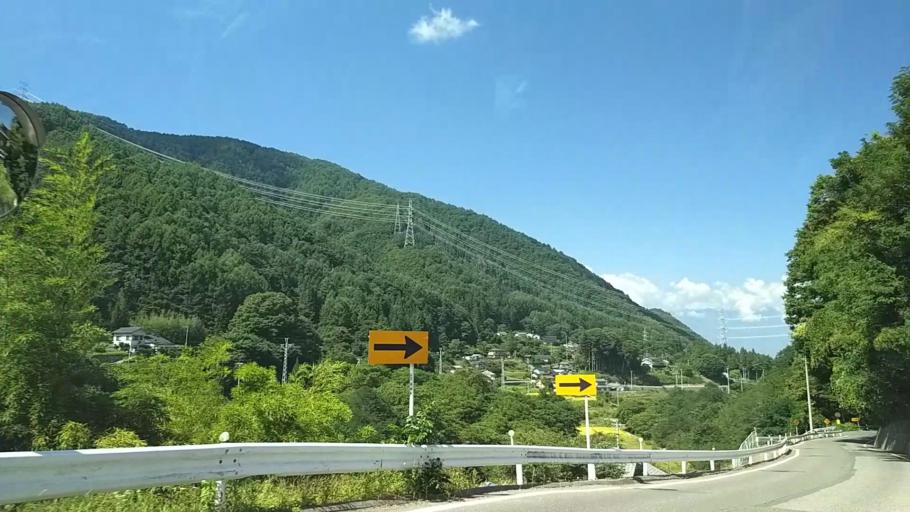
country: JP
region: Nagano
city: Matsumoto
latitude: 36.2198
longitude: 138.0434
